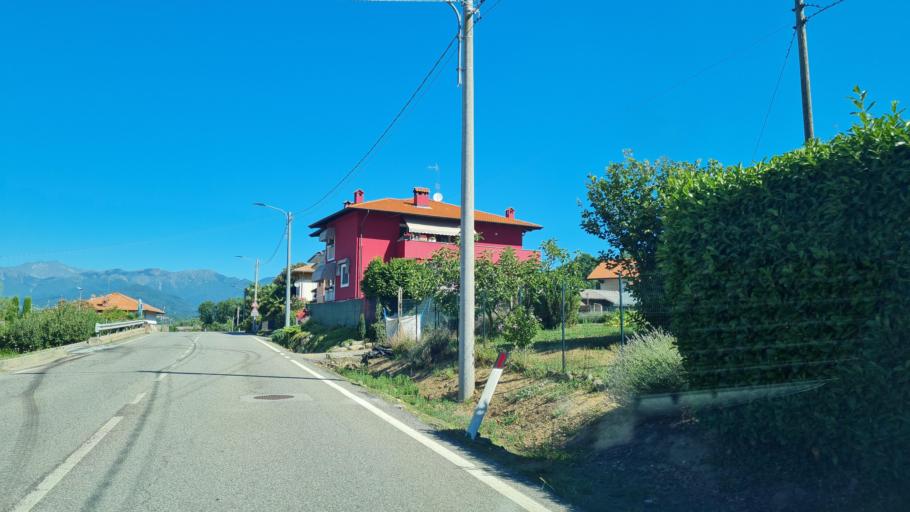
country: IT
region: Piedmont
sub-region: Provincia di Biella
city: Cossato
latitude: 45.5601
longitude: 8.2008
